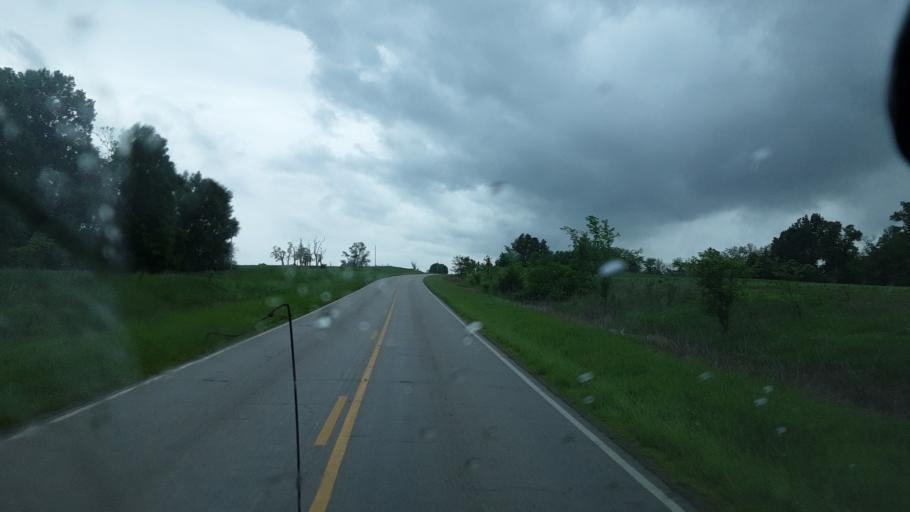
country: US
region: Missouri
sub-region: Monroe County
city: Paris
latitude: 39.4470
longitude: -92.2093
